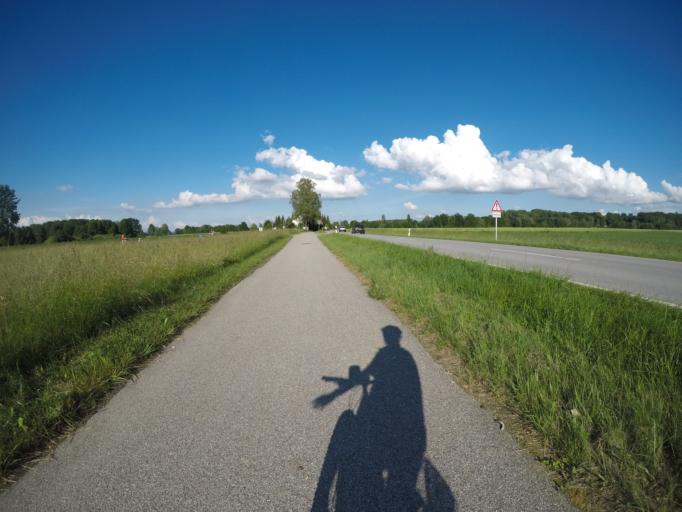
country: DE
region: Bavaria
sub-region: Lower Bavaria
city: Marklkofen
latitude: 48.5580
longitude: 12.5738
